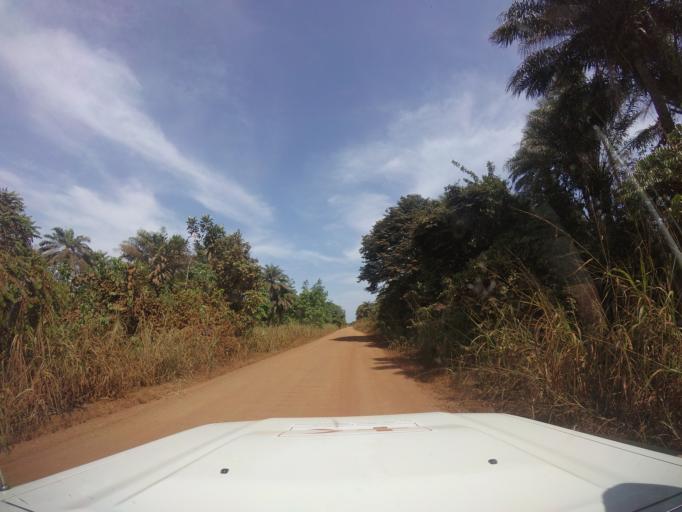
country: LR
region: Grand Cape Mount
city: Robertsport
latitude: 6.6854
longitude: -11.2457
